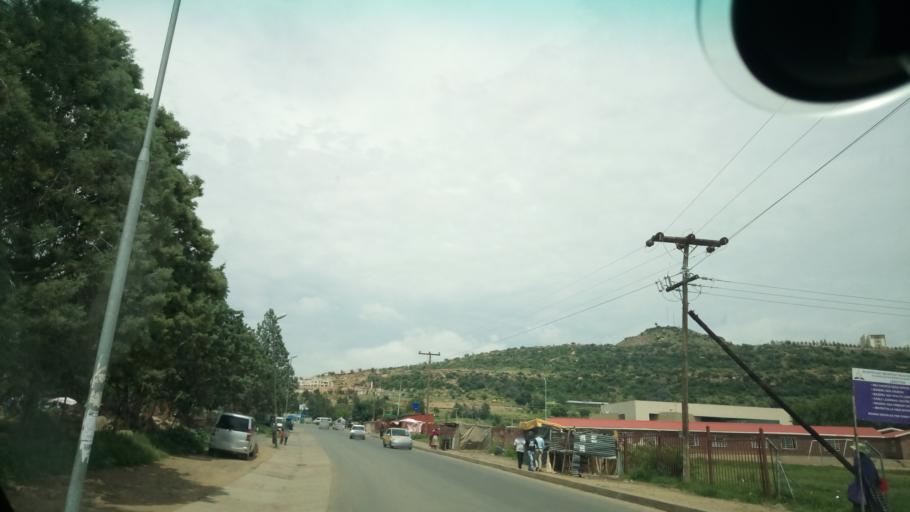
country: LS
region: Maseru
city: Maseru
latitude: -29.3227
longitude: 27.5014
